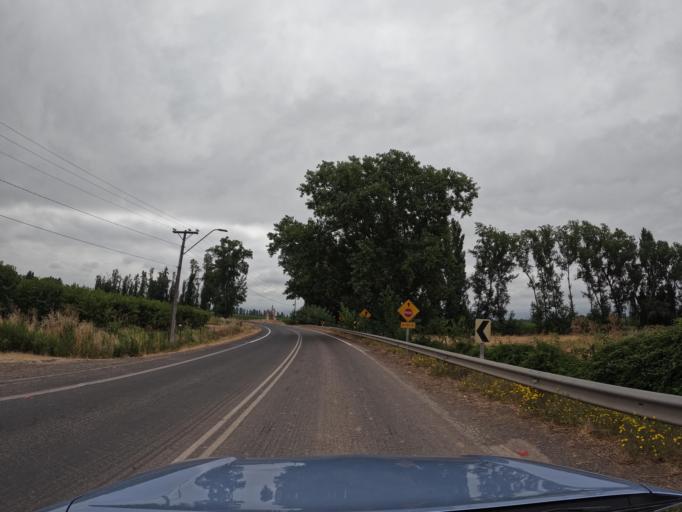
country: CL
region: O'Higgins
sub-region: Provincia de Colchagua
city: Chimbarongo
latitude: -34.7354
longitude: -71.0651
